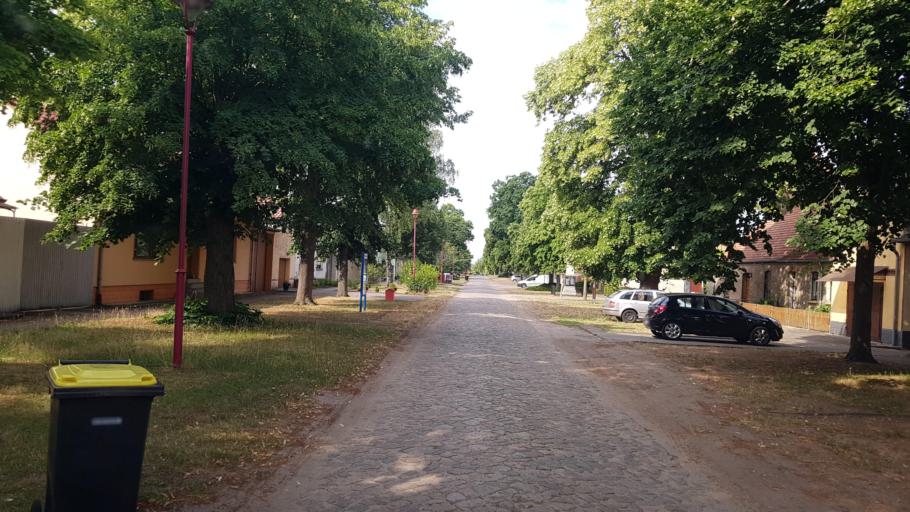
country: DE
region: Brandenburg
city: Bruck
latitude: 52.2308
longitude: 12.7194
